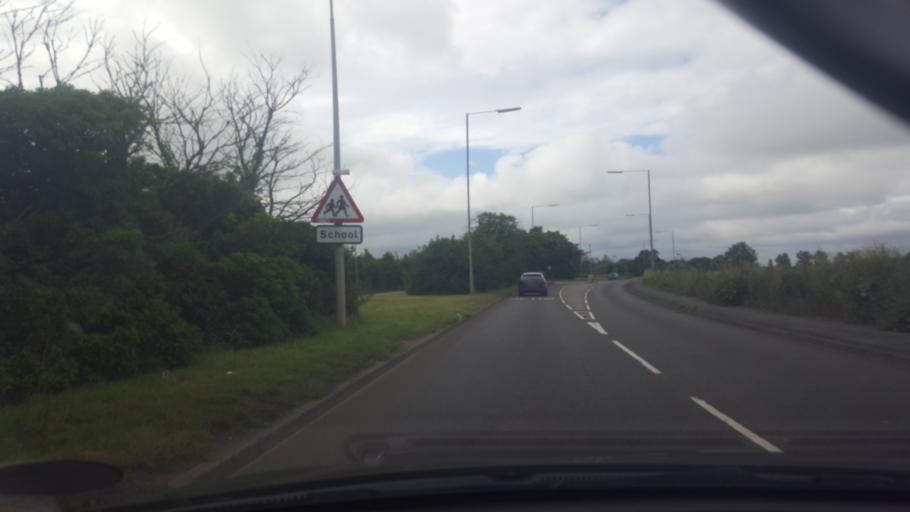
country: GB
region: England
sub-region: Essex
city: Clacton-on-Sea
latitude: 51.7945
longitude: 1.1198
